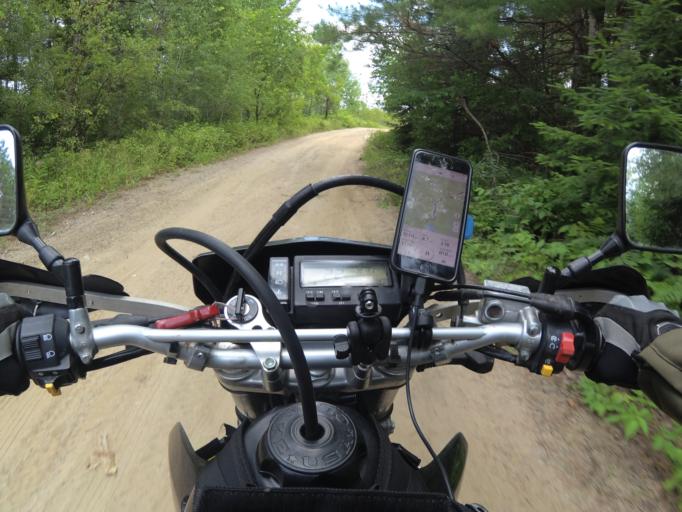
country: CA
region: Ontario
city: Bancroft
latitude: 45.0341
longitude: -77.2645
